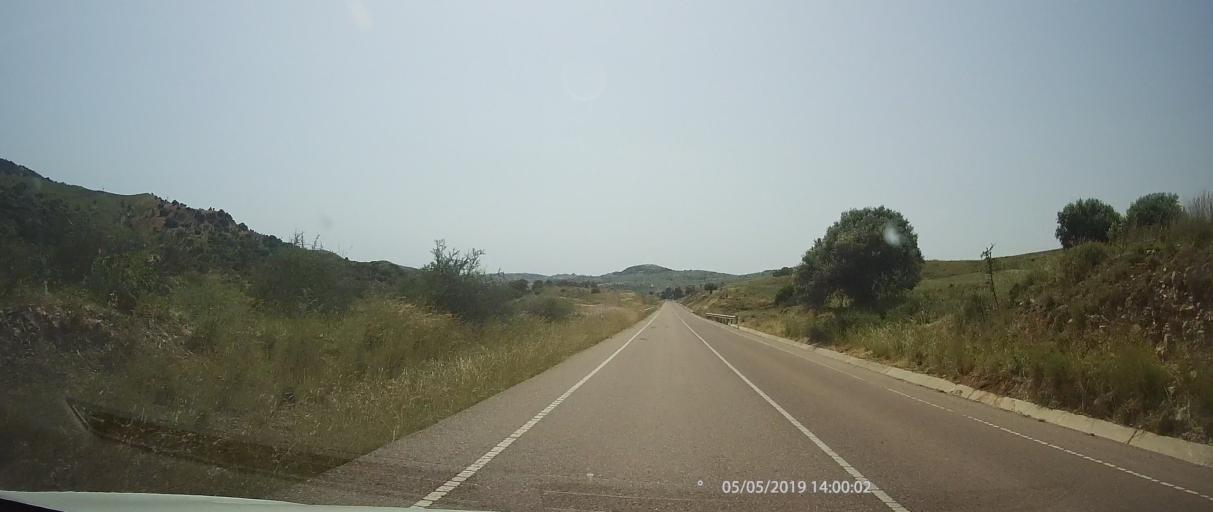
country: CY
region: Limassol
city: Pissouri
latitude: 34.7795
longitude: 32.6678
